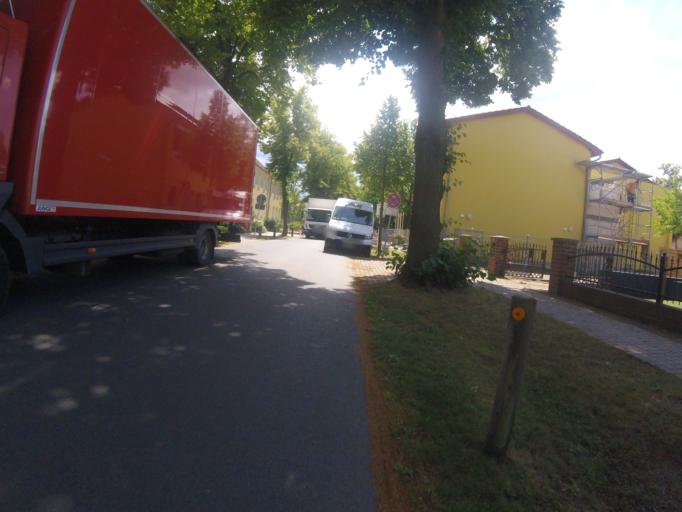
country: DE
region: Brandenburg
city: Bestensee
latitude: 52.2754
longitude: 13.6412
